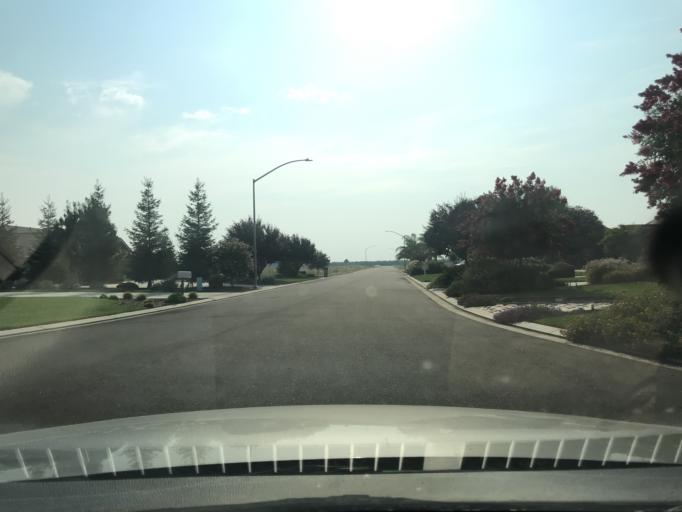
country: US
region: California
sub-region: Merced County
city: Atwater
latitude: 37.3176
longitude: -120.5972
